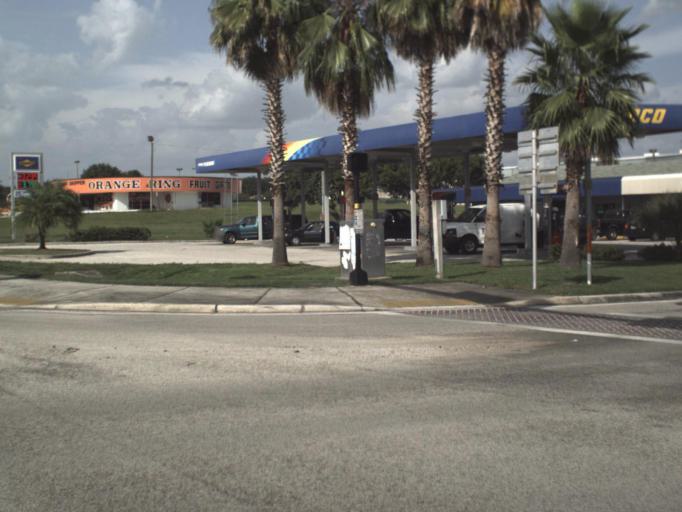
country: US
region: Florida
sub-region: Polk County
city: Haines City
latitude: 28.1213
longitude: -81.6396
